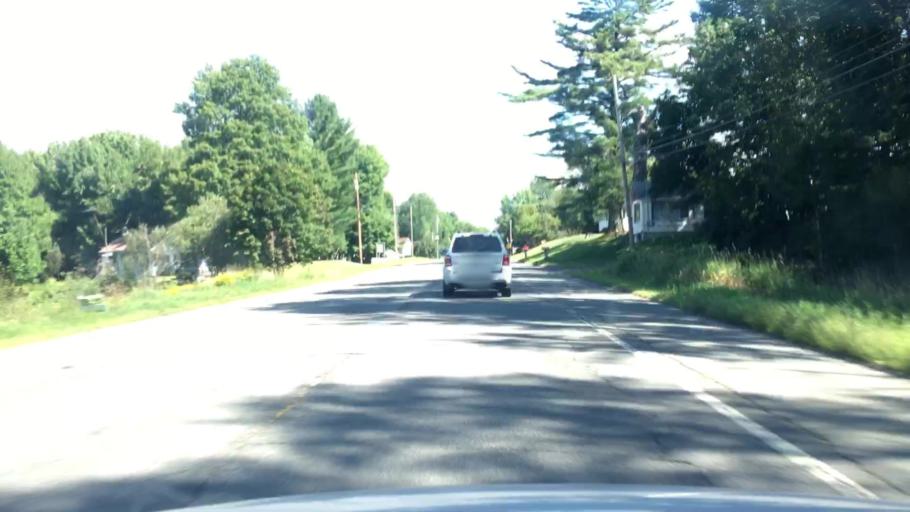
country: US
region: Maine
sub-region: Penobscot County
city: Dexter
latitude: 45.0446
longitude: -69.2729
